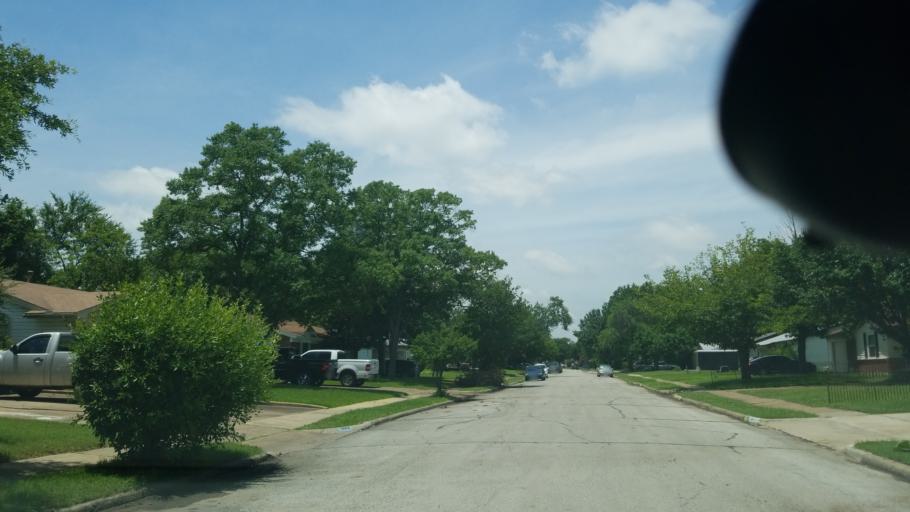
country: US
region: Texas
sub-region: Dallas County
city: Irving
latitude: 32.8481
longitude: -96.9683
